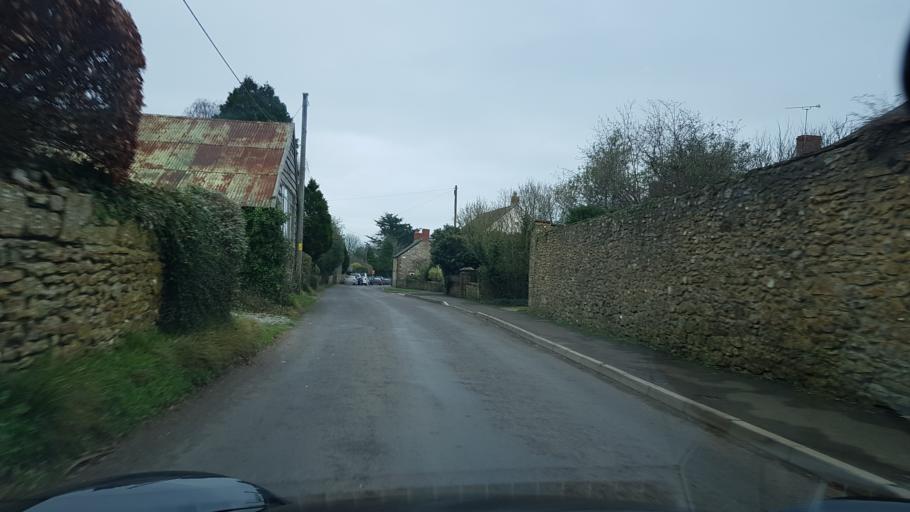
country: GB
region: England
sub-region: Somerset
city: Ilminster
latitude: 50.9345
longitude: -2.9662
